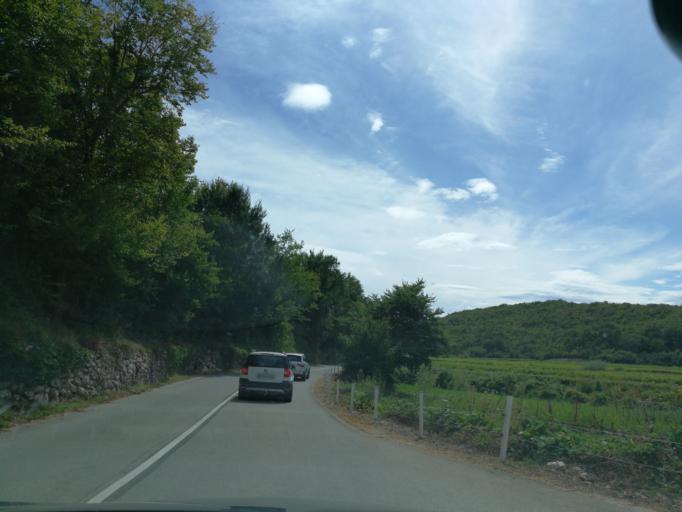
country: HR
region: Primorsko-Goranska
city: Punat
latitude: 45.0894
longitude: 14.6419
